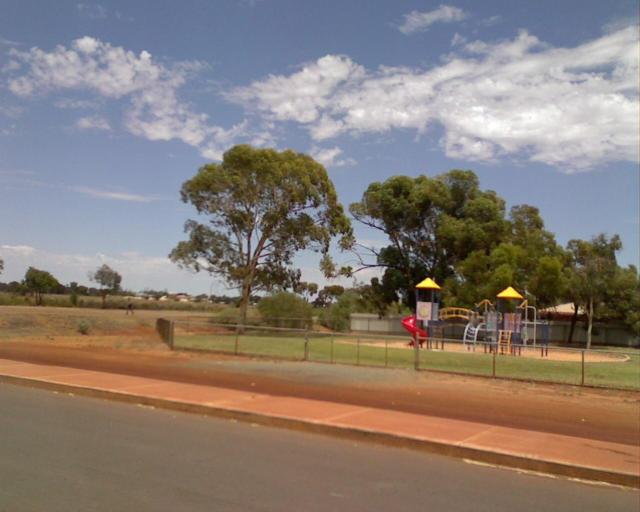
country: AU
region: Western Australia
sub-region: Kalgoorlie/Boulder
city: Boulder
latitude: -30.7759
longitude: 121.4603
